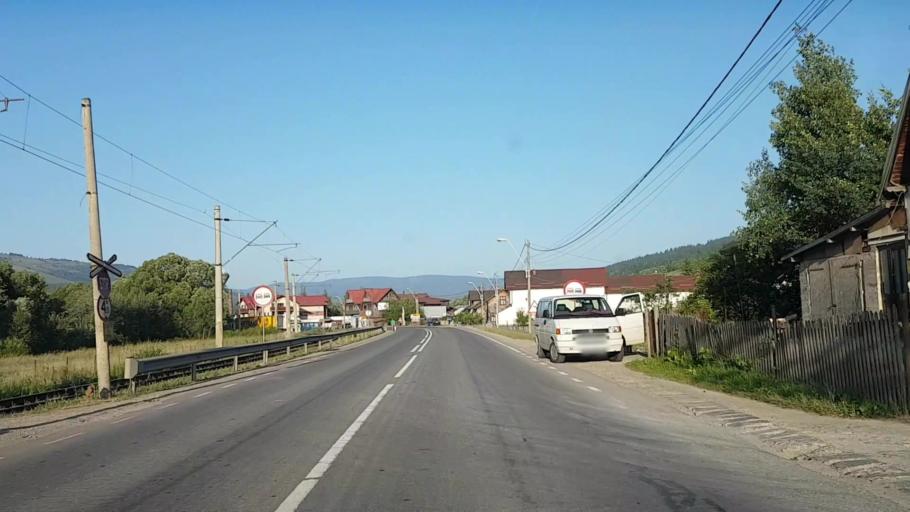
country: RO
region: Suceava
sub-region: Municipiul Vatra Dornei
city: Vatra Dornei
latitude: 47.3472
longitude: 25.3211
